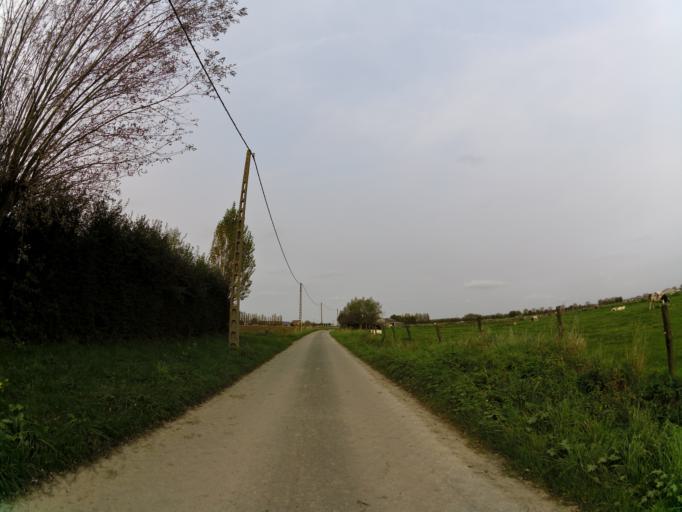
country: BE
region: Flanders
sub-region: Provincie West-Vlaanderen
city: Oudenburg
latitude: 51.2021
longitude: 3.0414
